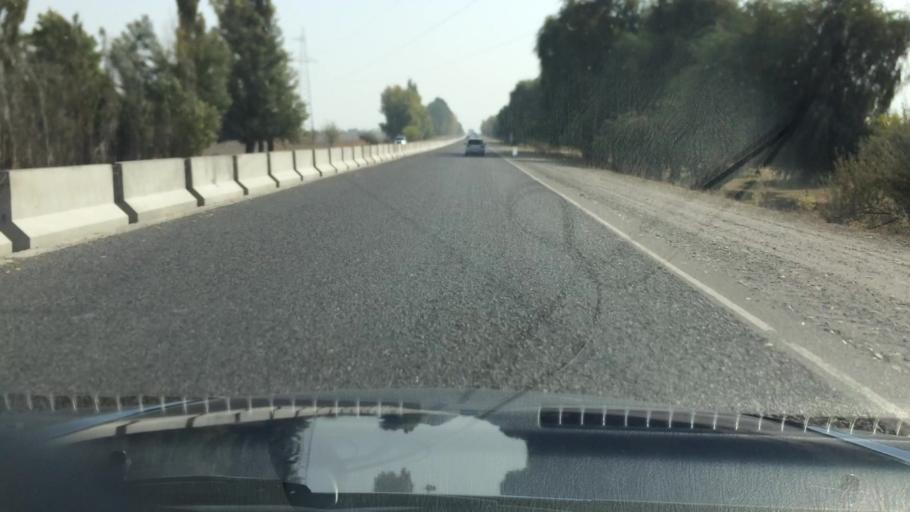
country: KG
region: Chuy
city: Kant
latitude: 42.9674
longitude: 74.9086
